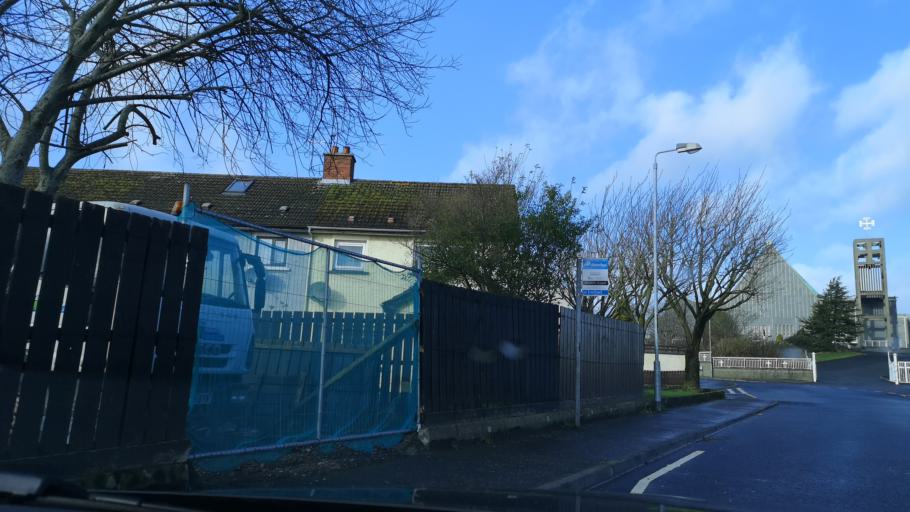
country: GB
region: Northern Ireland
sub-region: Newry and Mourne District
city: Newry
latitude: 54.1846
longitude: -6.3494
